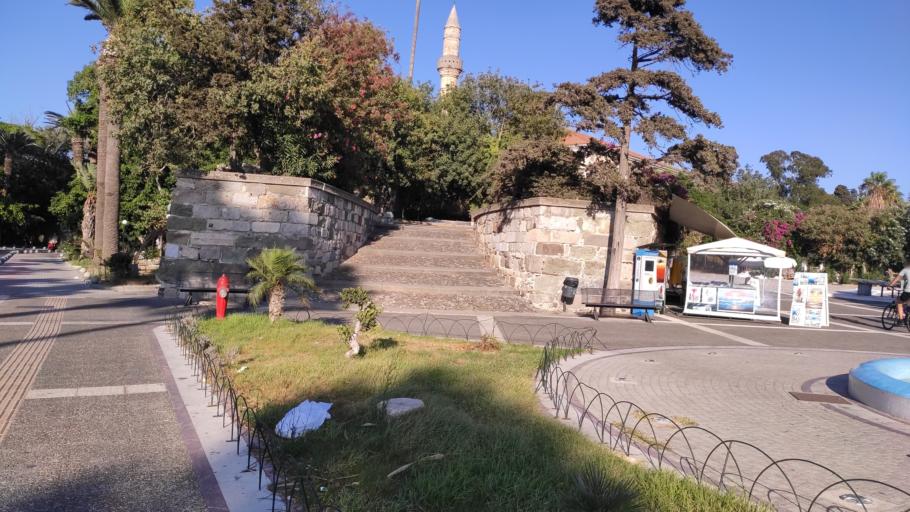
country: GR
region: South Aegean
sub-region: Nomos Dodekanisou
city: Kos
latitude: 36.8945
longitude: 27.2900
